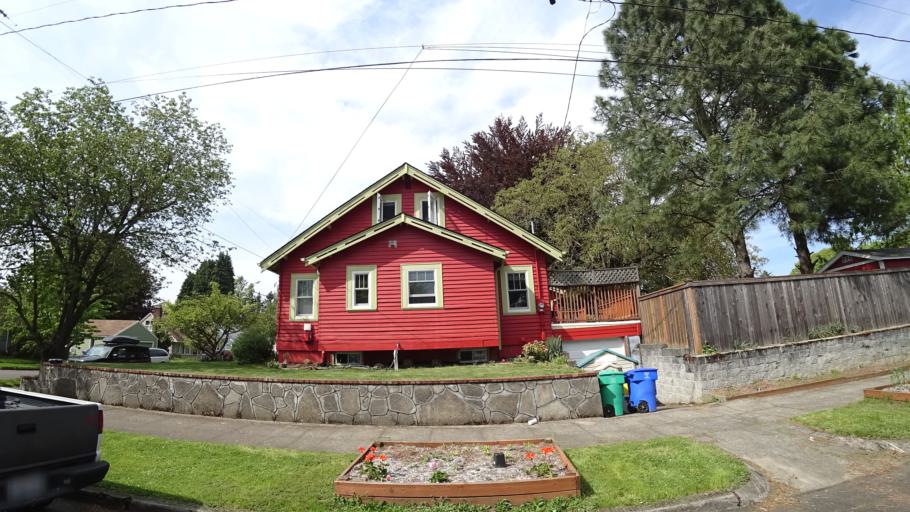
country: US
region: Oregon
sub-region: Clackamas County
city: Milwaukie
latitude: 45.4821
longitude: -122.6161
